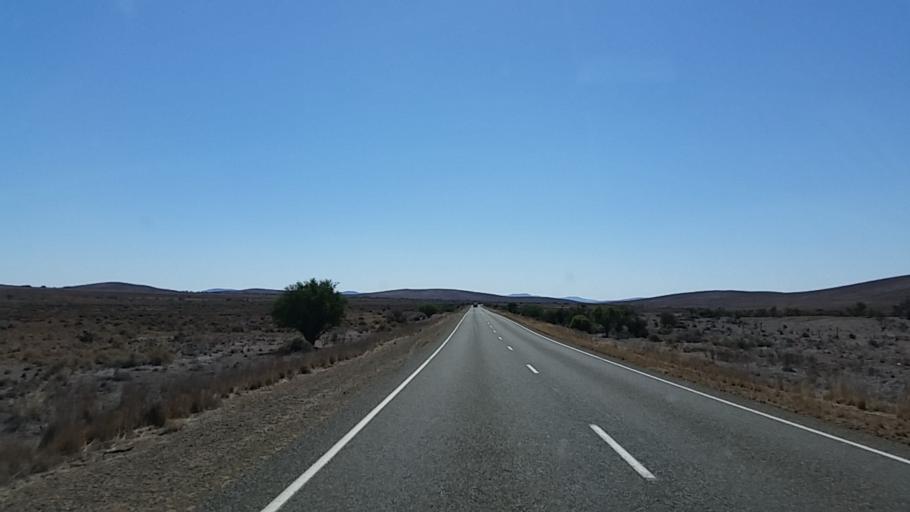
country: AU
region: South Australia
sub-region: Flinders Ranges
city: Quorn
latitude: -32.1559
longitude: 138.5274
